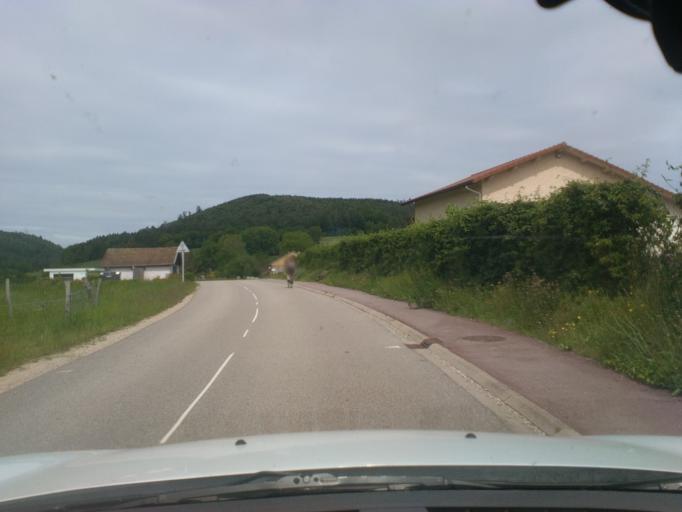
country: FR
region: Lorraine
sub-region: Departement des Vosges
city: Le Tholy
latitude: 48.1378
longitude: 6.6991
